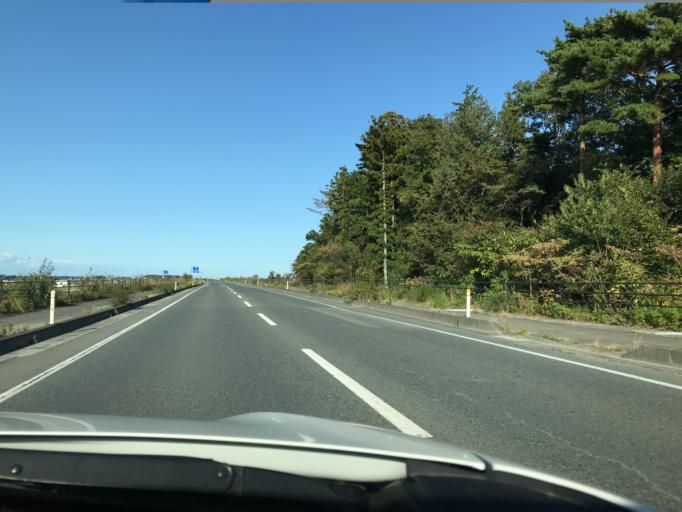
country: JP
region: Miyagi
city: Marumori
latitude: 37.7833
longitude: 140.9419
